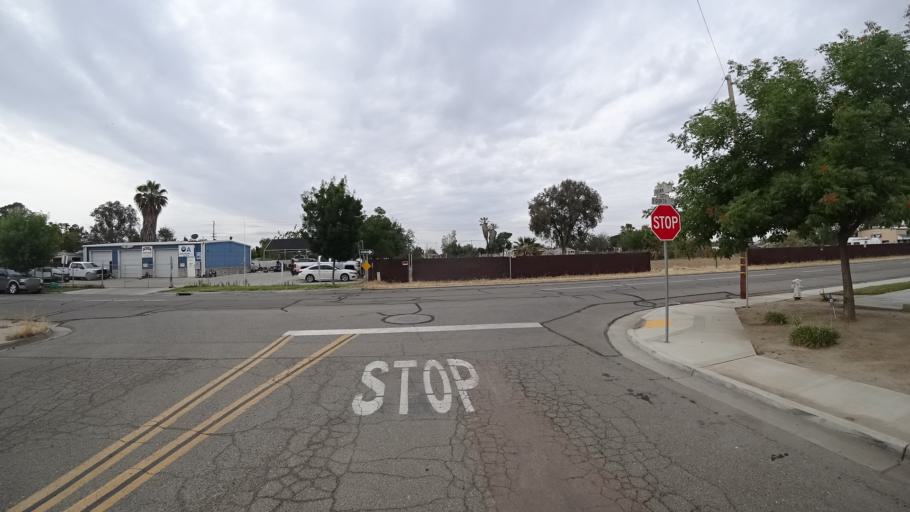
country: US
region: California
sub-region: Kings County
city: Hanford
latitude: 36.3243
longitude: -119.6418
